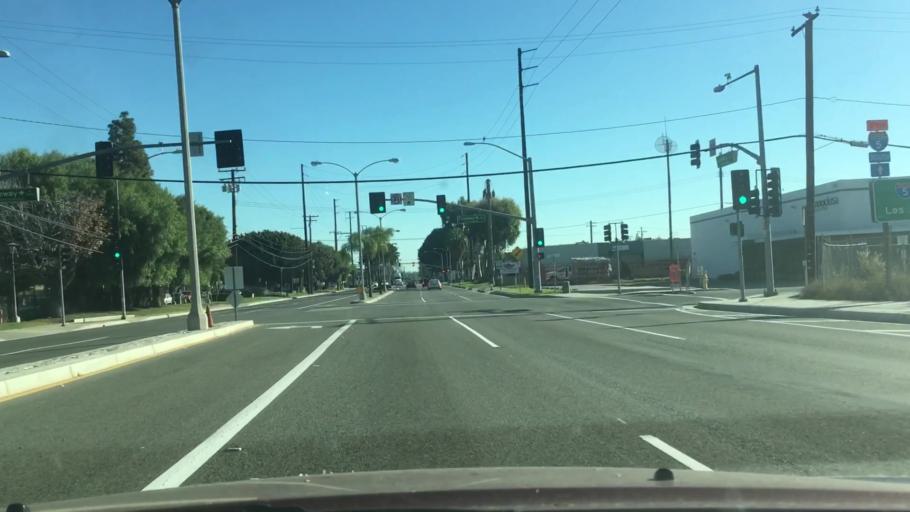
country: US
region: California
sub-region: Los Angeles County
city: La Mirada
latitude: 33.8879
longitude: -118.0319
